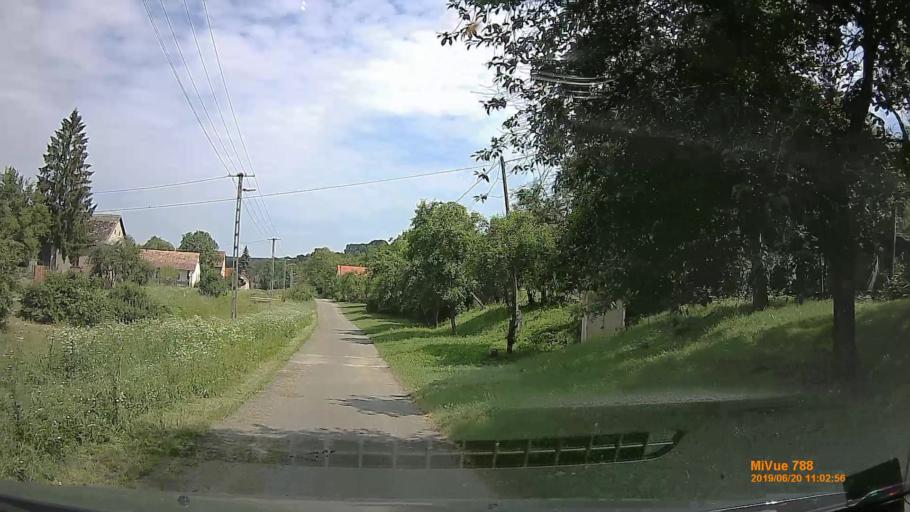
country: HU
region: Baranya
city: Mecseknadasd
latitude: 46.1799
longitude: 18.5120
